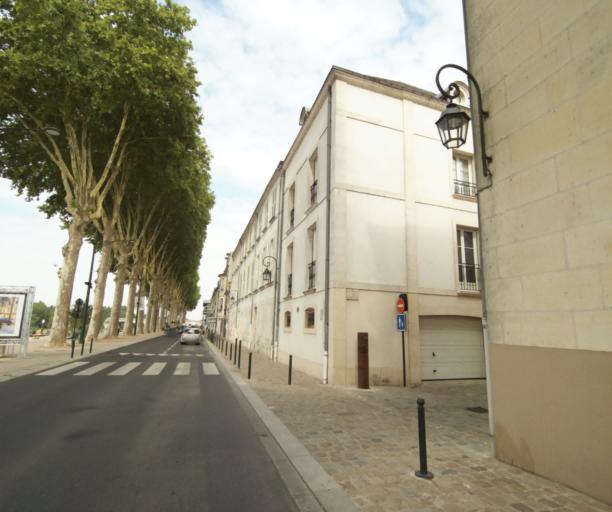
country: FR
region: Centre
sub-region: Departement du Loiret
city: Saint-Jean-le-Blanc
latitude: 47.8980
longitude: 1.9110
